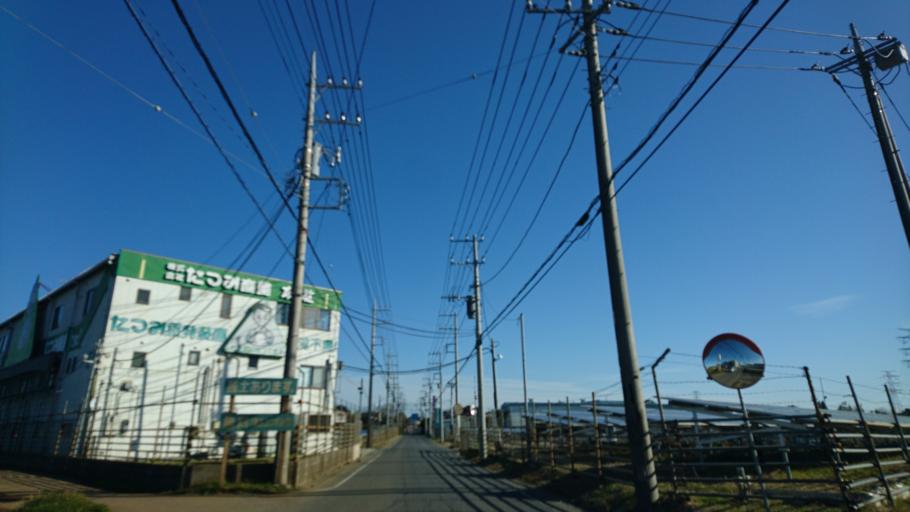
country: JP
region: Chiba
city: Togane
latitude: 35.5868
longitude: 140.3172
